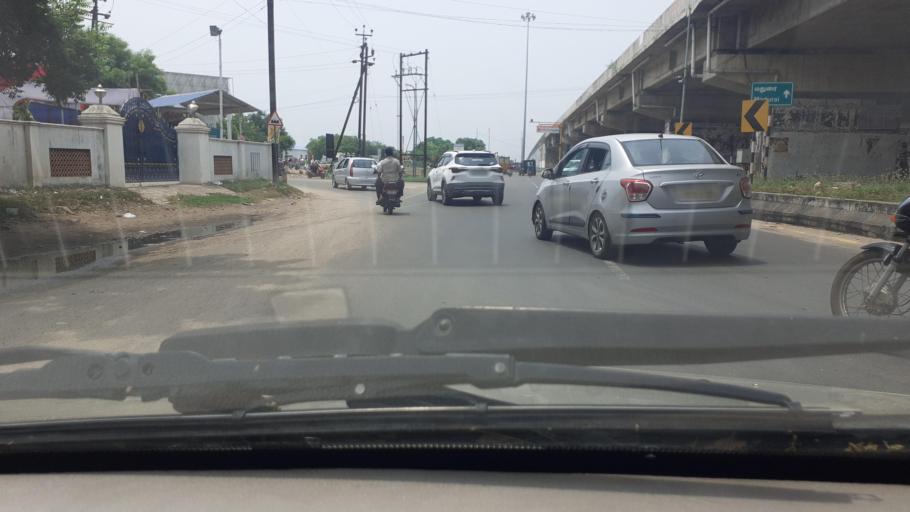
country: IN
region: Tamil Nadu
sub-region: Tirunelveli Kattabo
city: Tirunelveli
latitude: 8.7135
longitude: 77.7651
